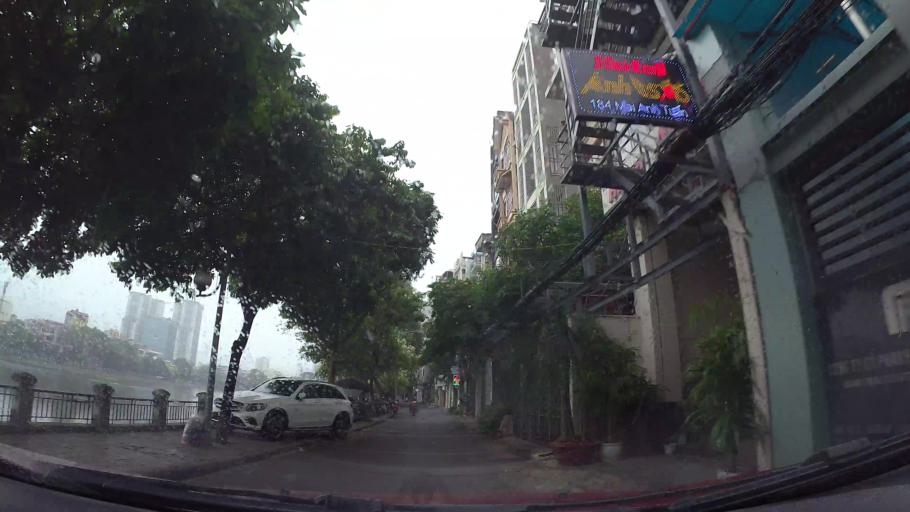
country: VN
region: Ha Noi
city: Dong Da
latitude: 21.0190
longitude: 105.8192
